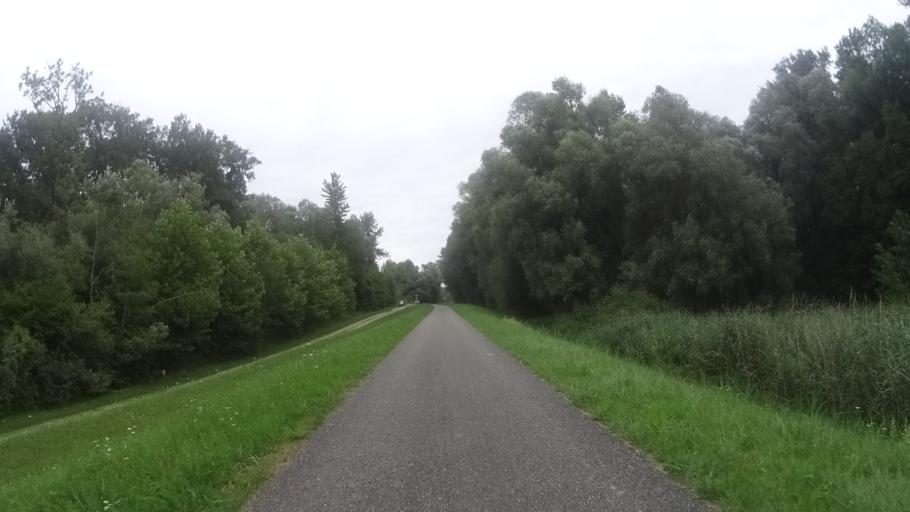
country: DE
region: Rheinland-Pfalz
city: Berg
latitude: 48.9450
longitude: 8.1841
